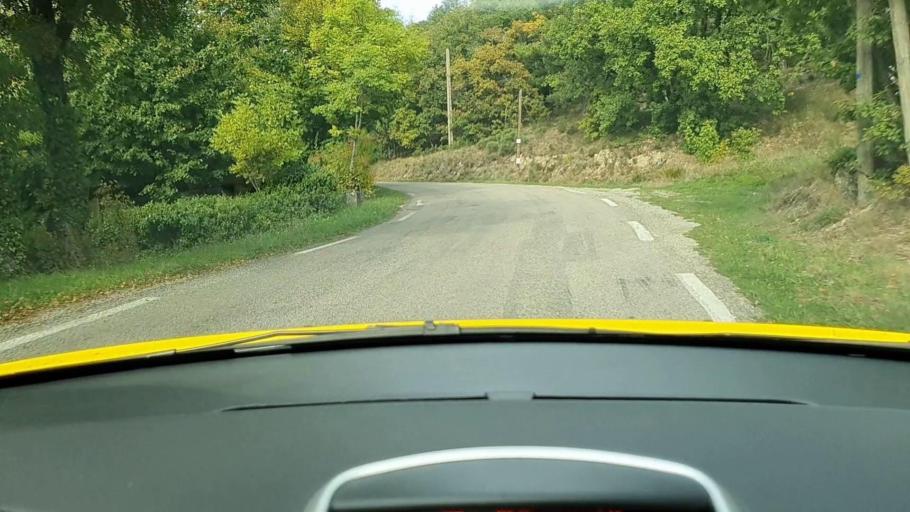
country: FR
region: Languedoc-Roussillon
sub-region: Departement du Gard
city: Le Vigan
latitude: 44.0215
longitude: 3.5728
